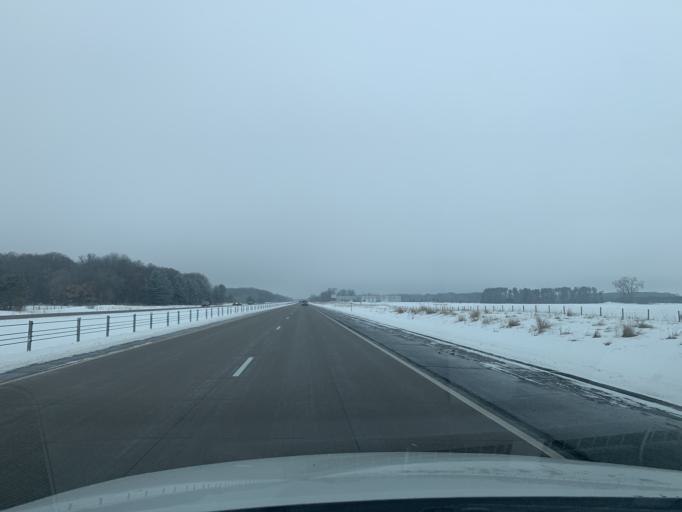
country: US
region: Minnesota
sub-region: Chisago County
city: North Branch
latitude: 45.5339
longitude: -92.9906
